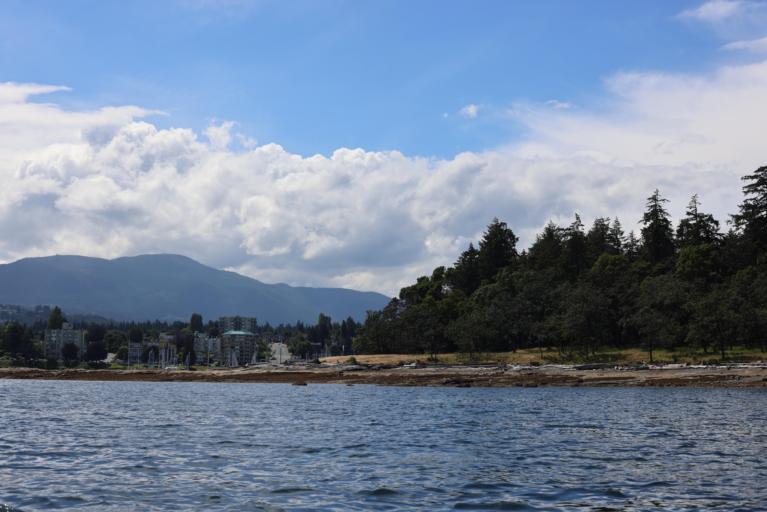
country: CA
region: British Columbia
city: Nanaimo
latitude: 49.1786
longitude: -123.9325
